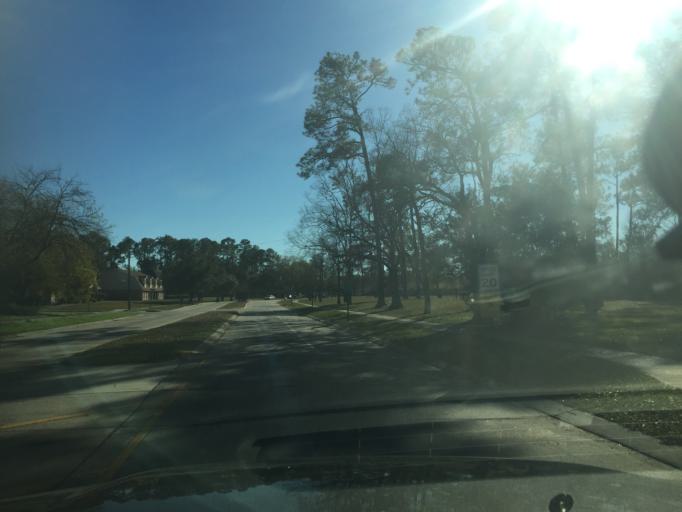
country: US
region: Louisiana
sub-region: Saint Tammany Parish
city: Slidell
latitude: 30.2922
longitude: -89.7581
